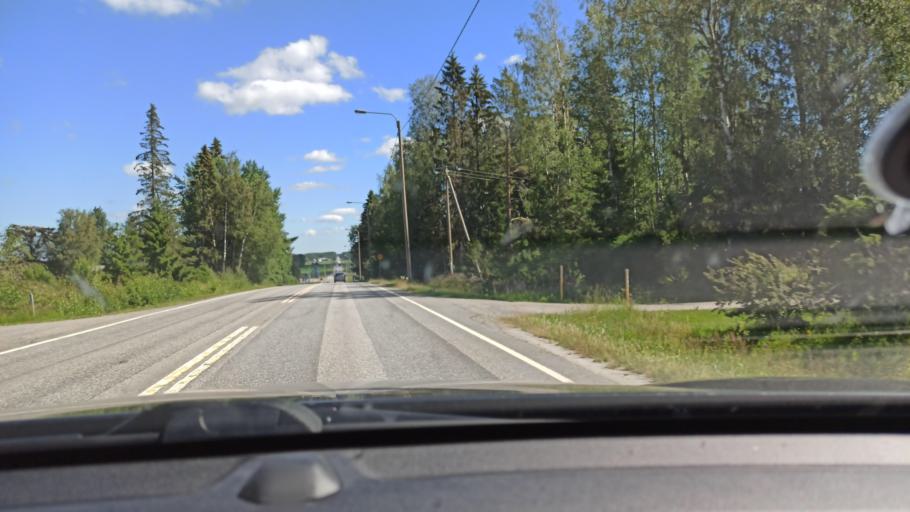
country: FI
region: Ostrobothnia
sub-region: Vaasa
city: Teeriniemi
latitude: 62.9985
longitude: 21.6654
